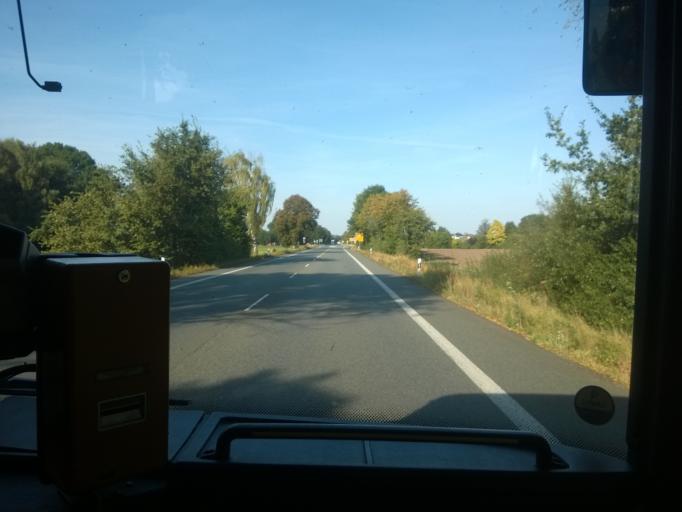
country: DE
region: North Rhine-Westphalia
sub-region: Regierungsbezirk Munster
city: Sudlohn
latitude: 51.9298
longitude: 6.8530
